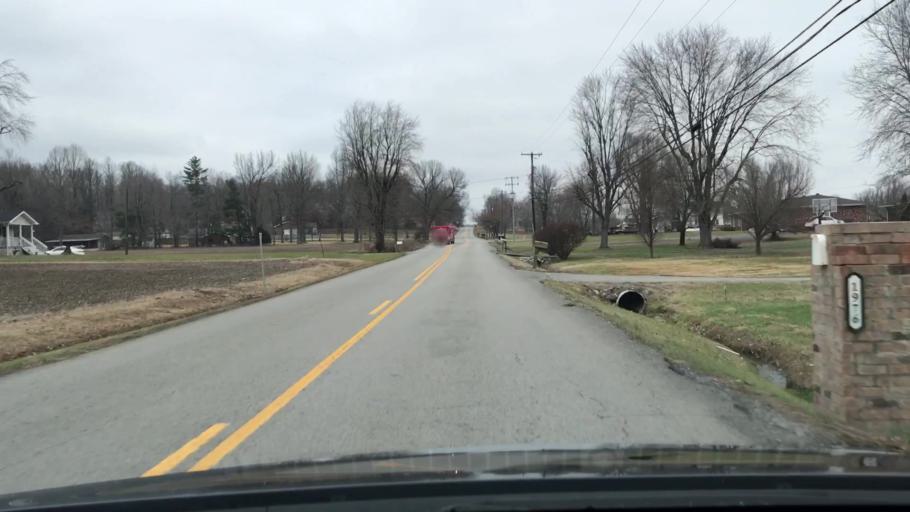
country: US
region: Kentucky
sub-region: Muhlenberg County
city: Greenville
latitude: 37.2224
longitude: -87.1937
